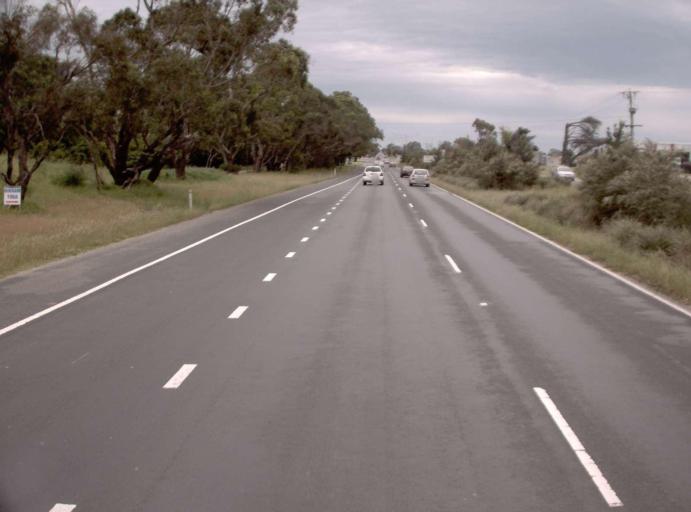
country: AU
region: Victoria
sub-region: Casey
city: Hampton Park
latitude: -38.0385
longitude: 145.2496
